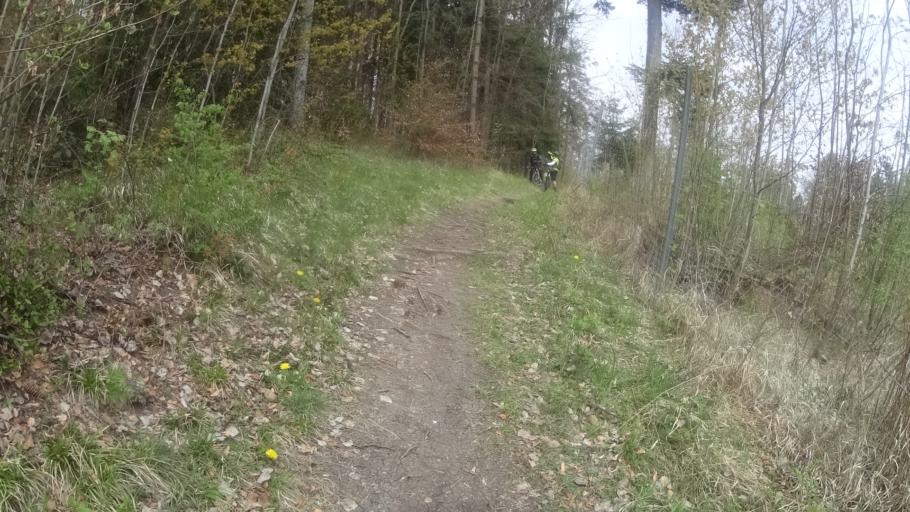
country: DE
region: Bavaria
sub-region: Upper Franconia
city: Igensdorf
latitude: 49.6269
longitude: 11.2014
